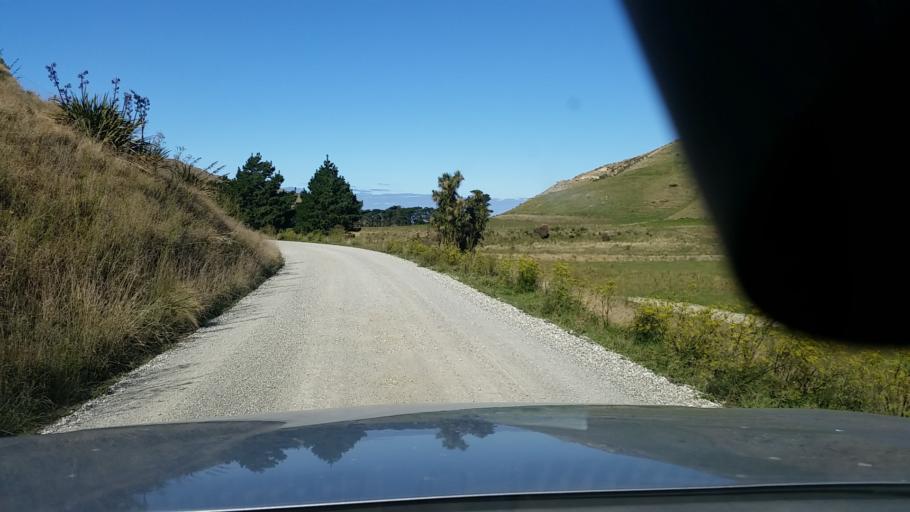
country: NZ
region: Marlborough
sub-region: Marlborough District
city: Blenheim
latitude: -41.8362
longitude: 174.1765
